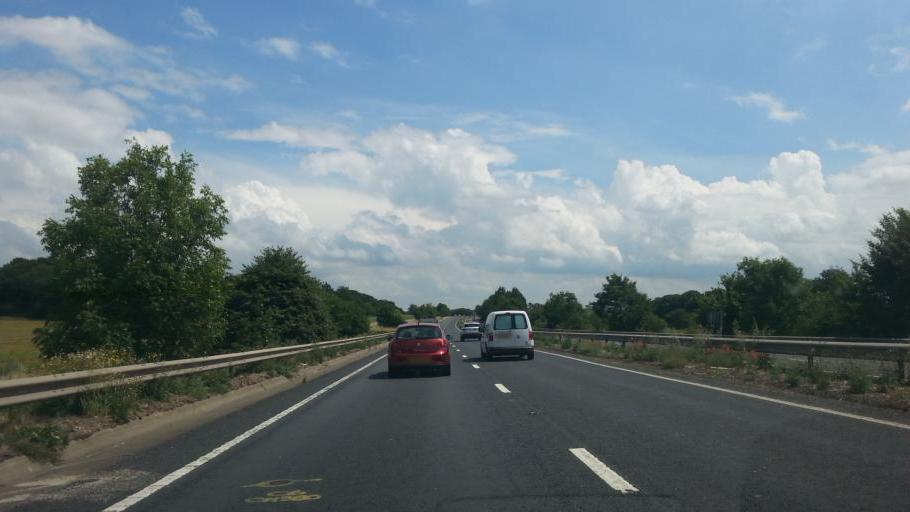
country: GB
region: England
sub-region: Norfolk
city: Thetford
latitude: 52.4342
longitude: 0.7610
